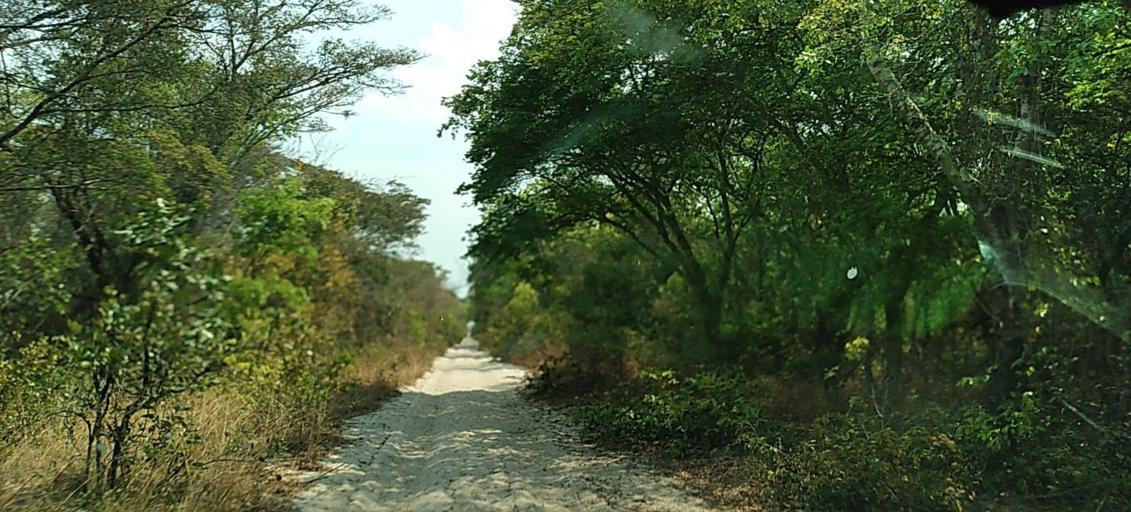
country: ZM
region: North-Western
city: Kabompo
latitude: -13.3880
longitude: 23.7648
